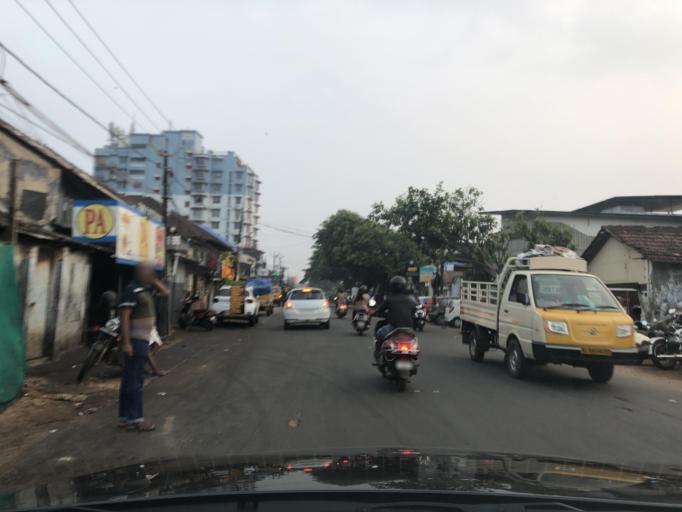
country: IN
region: Kerala
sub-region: Kozhikode
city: Kozhikode
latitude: 11.2482
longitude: 75.7726
